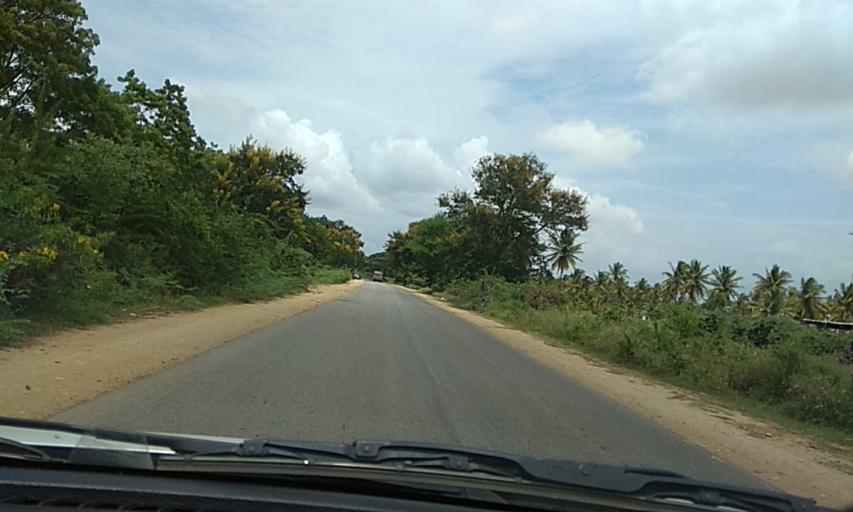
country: IN
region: Karnataka
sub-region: Chamrajnagar
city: Gundlupet
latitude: 11.8110
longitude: 76.7304
